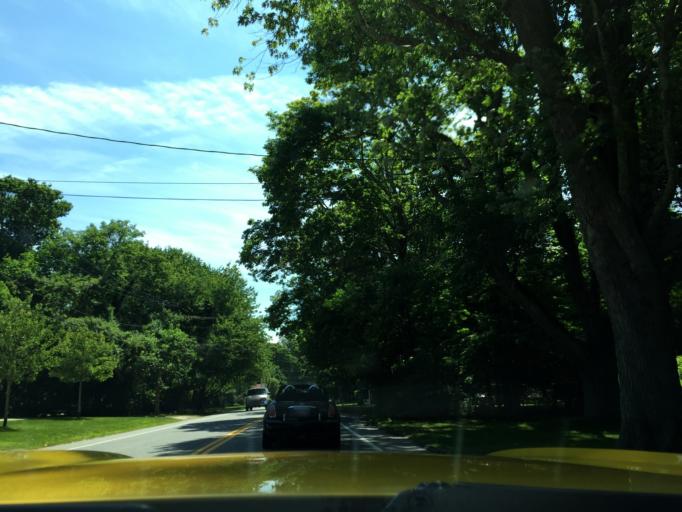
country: US
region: New York
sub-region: Suffolk County
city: Bridgehampton
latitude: 40.9324
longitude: -72.3046
